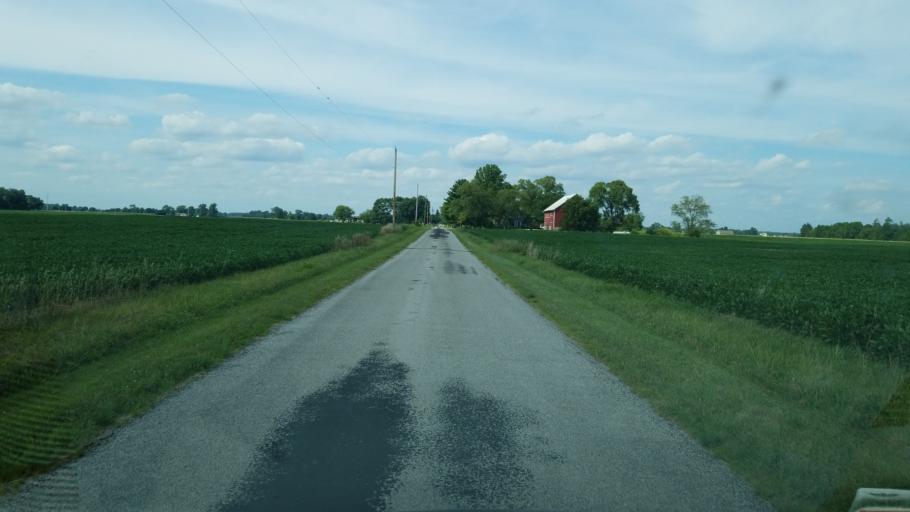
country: US
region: Ohio
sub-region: Marion County
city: Prospect
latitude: 40.4620
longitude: -83.1248
